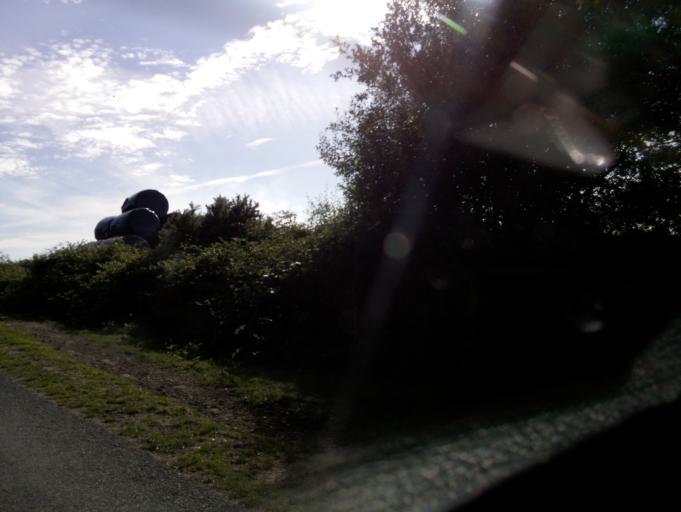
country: GB
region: England
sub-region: Hampshire
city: West Wellow
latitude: 50.9516
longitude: -1.5863
